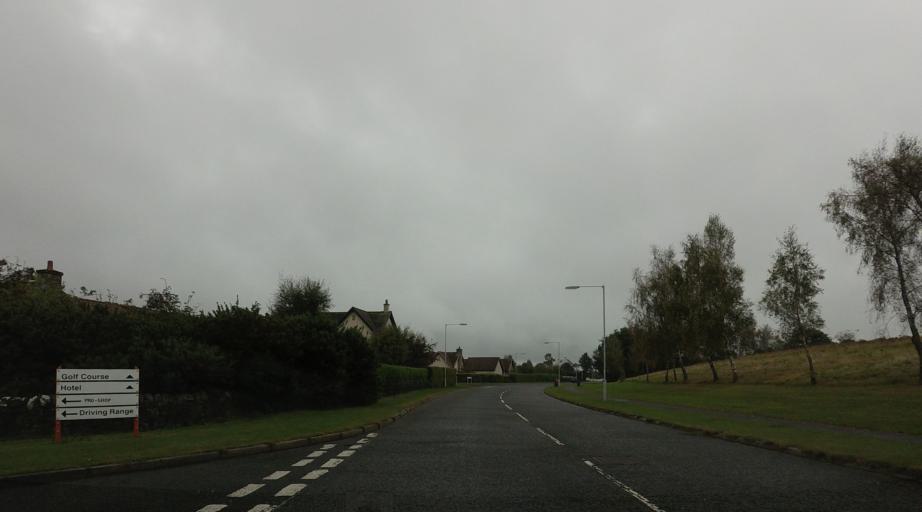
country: GB
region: Scotland
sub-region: Fife
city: Newport-On-Tay
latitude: 56.4154
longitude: -2.9124
